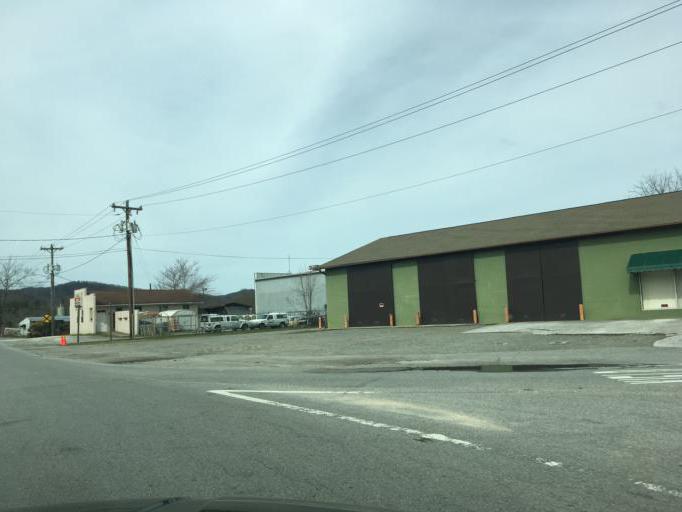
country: US
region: North Carolina
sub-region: Transylvania County
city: Brevard
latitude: 35.2539
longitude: -82.7003
